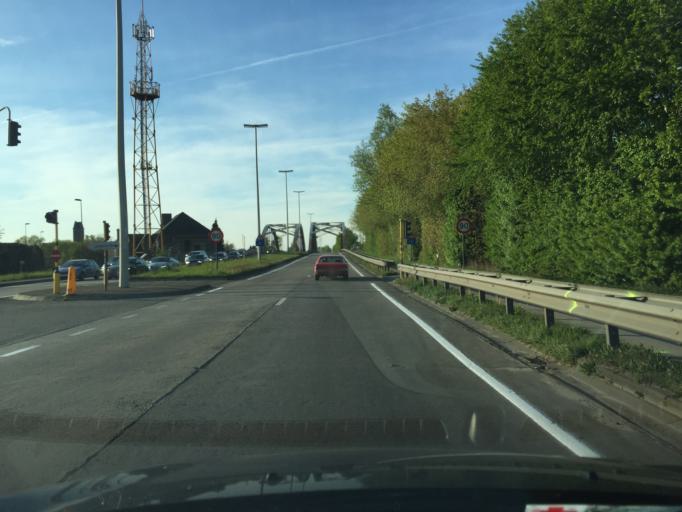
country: BE
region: Flanders
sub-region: Provincie Oost-Vlaanderen
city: Aalter
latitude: 51.1053
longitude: 3.4355
